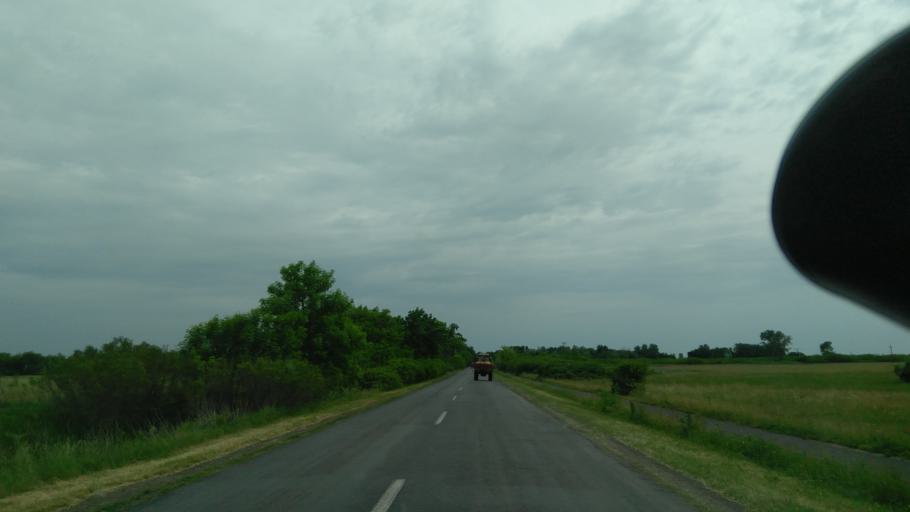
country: HU
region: Bekes
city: Sarkad
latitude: 46.7711
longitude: 21.3819
